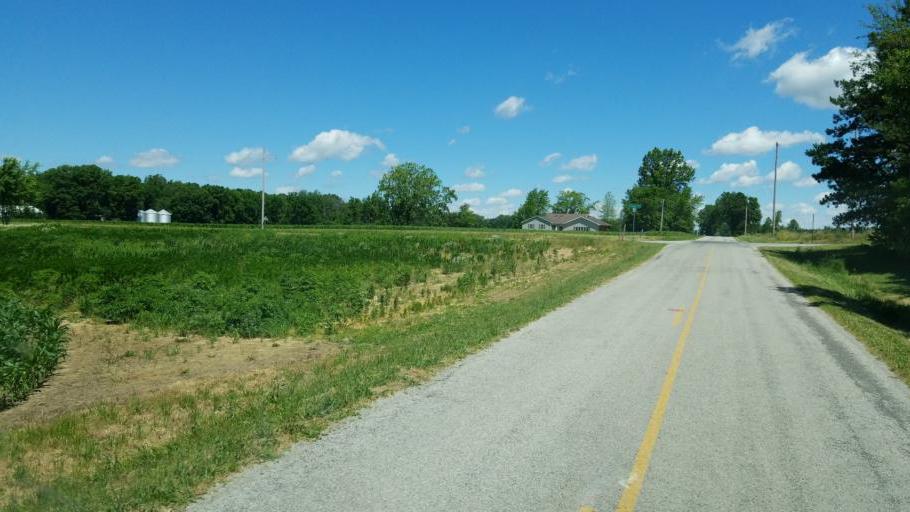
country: US
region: Ohio
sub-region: Crawford County
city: Bucyrus
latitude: 40.6659
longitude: -82.9388
